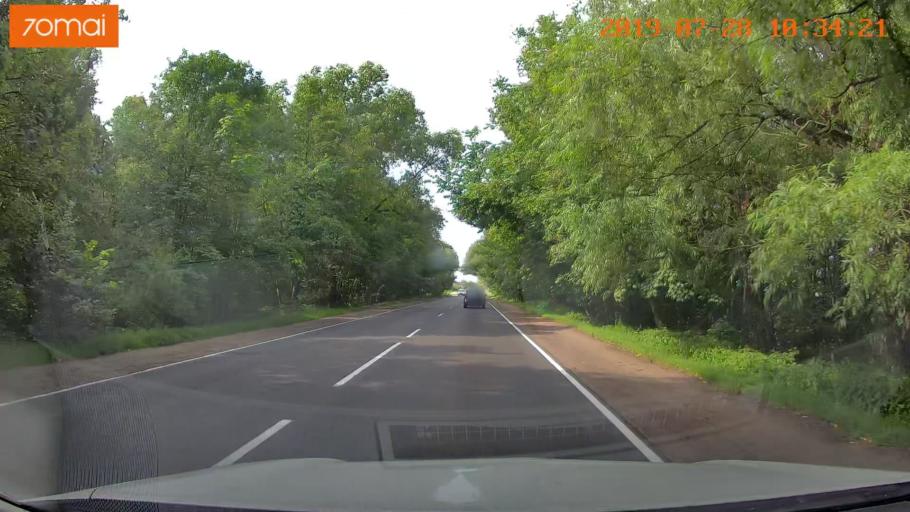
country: RU
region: Kaliningrad
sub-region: Gorod Kaliningrad
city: Kaliningrad
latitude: 54.7542
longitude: 20.4401
